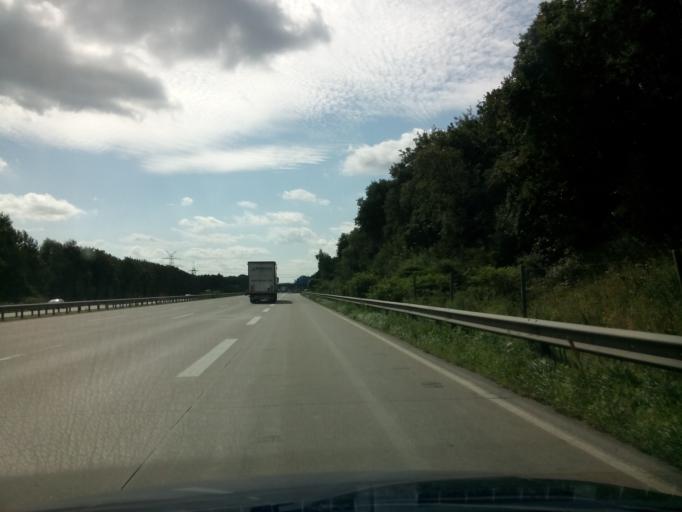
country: DE
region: Lower Saxony
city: Ritterhude
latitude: 53.1511
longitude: 8.7278
